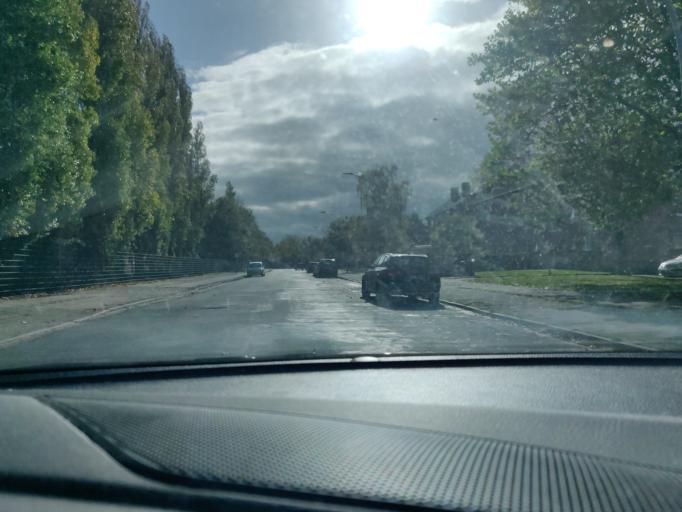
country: DE
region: Lower Saxony
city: Cuxhaven
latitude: 53.8510
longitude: 8.6868
